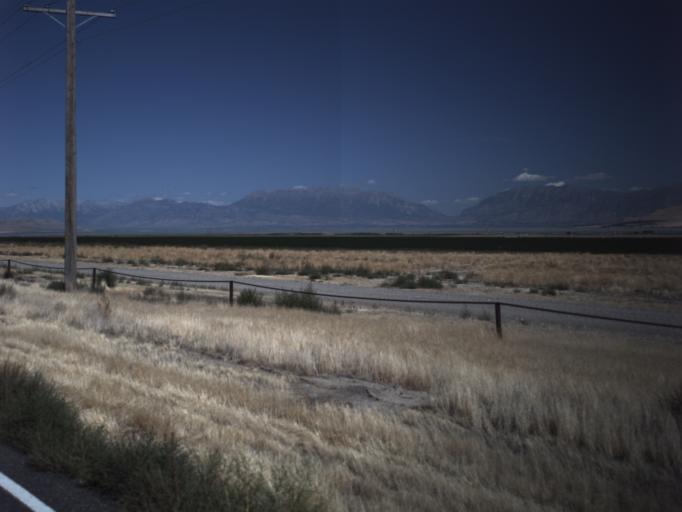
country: US
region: Utah
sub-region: Utah County
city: Genola
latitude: 40.0558
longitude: -111.9583
